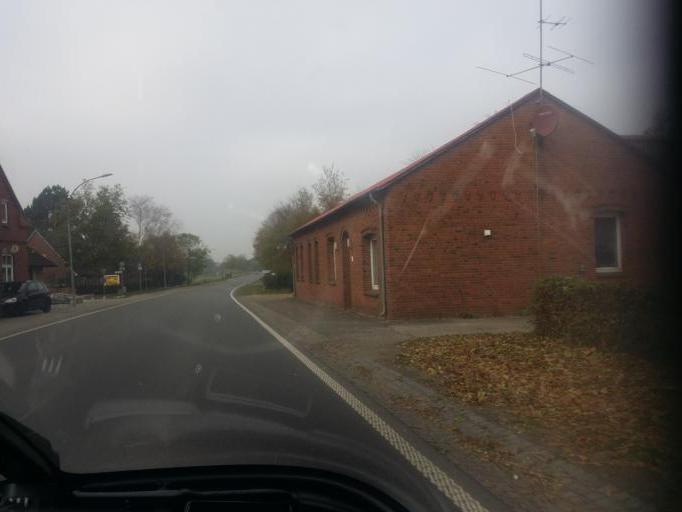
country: DE
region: Schleswig-Holstein
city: Bordelum
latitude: 54.6318
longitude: 8.9374
